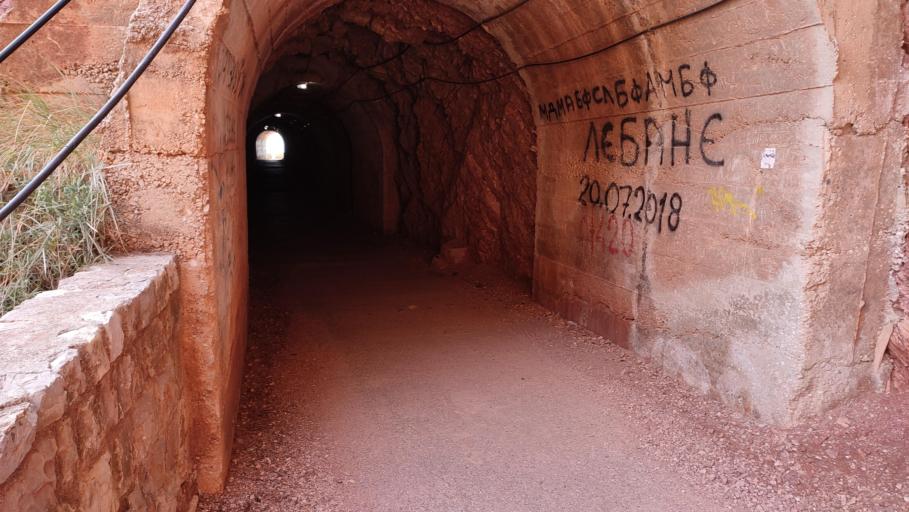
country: ME
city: Petrovac na Moru
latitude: 42.2078
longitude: 18.9287
